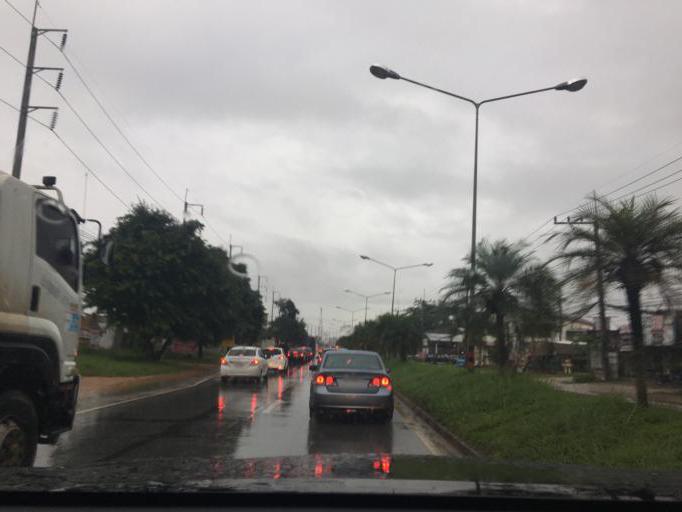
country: TH
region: Chiang Rai
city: Mae Chan
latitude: 20.0529
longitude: 99.8756
